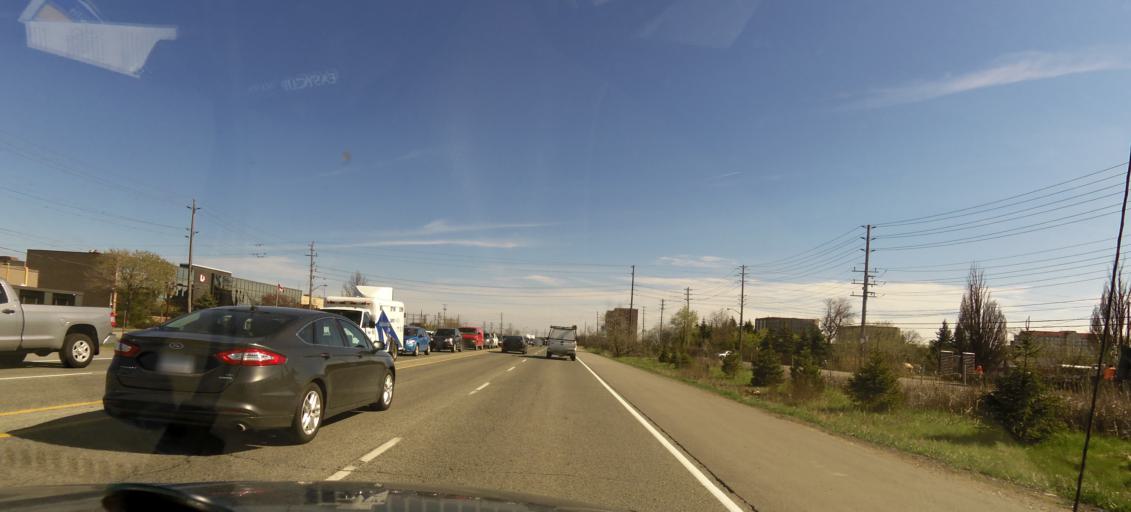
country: CA
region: Ontario
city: Etobicoke
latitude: 43.6948
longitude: -79.5851
